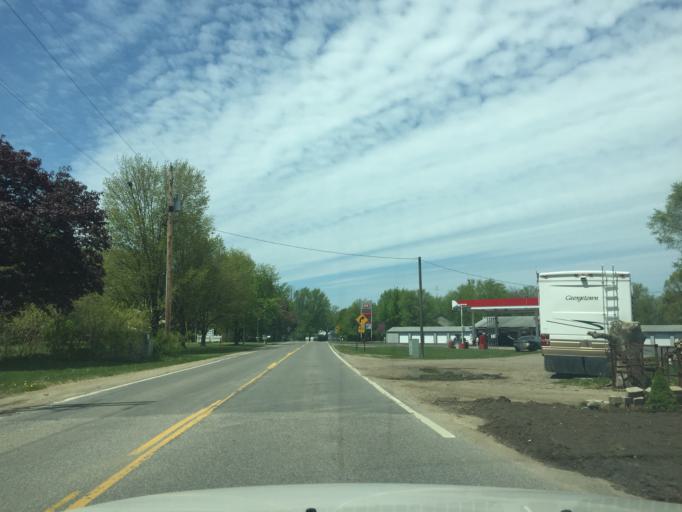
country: US
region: Michigan
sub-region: Berrien County
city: Stevensville
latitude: 41.9769
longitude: -86.4949
